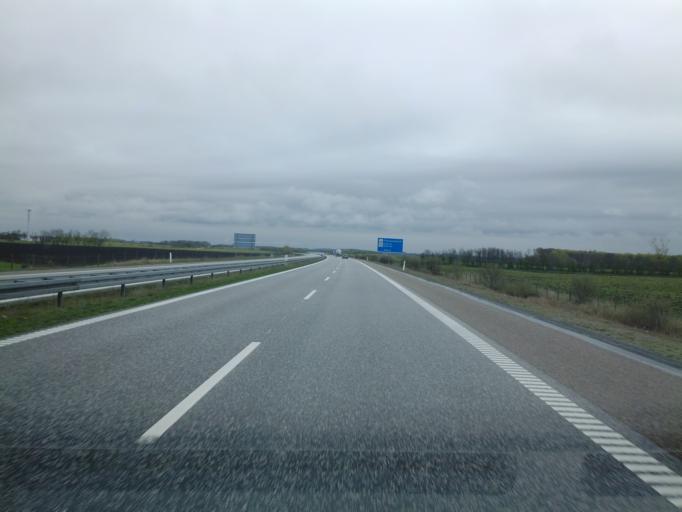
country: DK
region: North Denmark
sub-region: Bronderslev Kommune
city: Dronninglund
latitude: 57.2430
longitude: 10.3149
